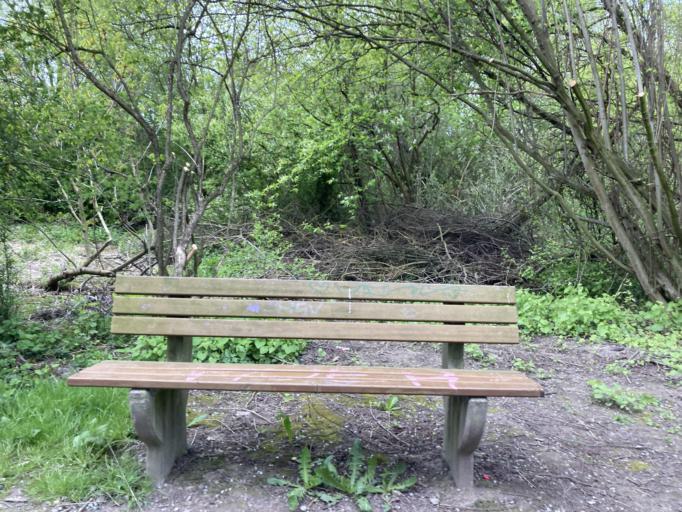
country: DE
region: Lower Saxony
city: Sarstedt
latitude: 52.2766
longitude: 9.8291
